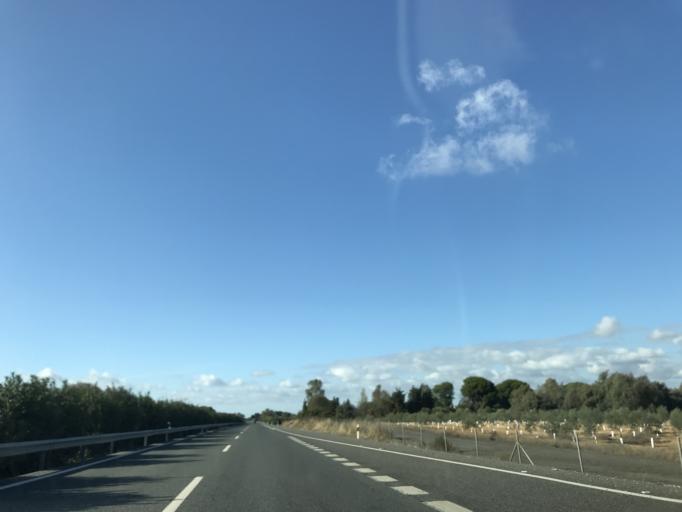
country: ES
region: Andalusia
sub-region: Provincia de Sevilla
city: Marchena
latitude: 37.2574
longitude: -5.4139
